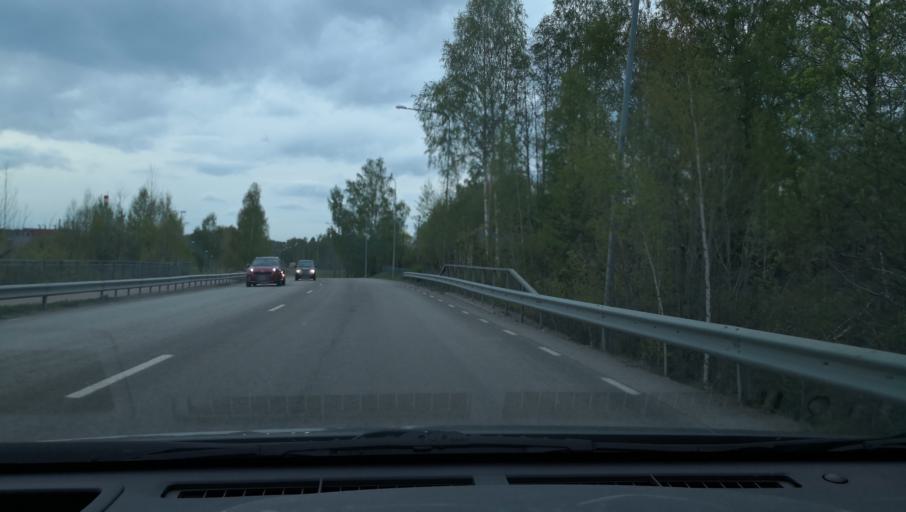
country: SE
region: Dalarna
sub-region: Avesta Kommun
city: Avesta
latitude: 60.1367
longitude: 16.2087
